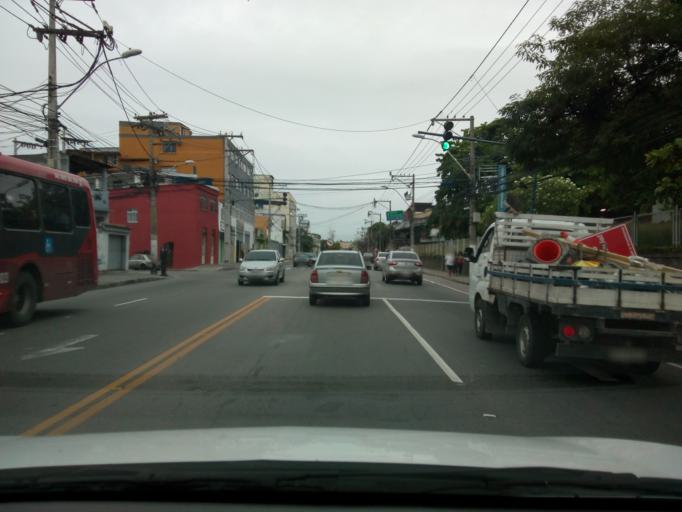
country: BR
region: Rio de Janeiro
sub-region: Niteroi
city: Niteroi
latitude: -22.8764
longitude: -43.1079
